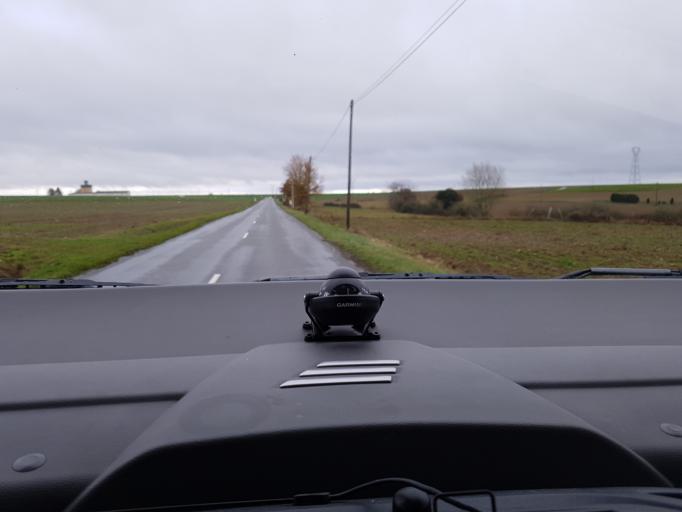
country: FR
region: Haute-Normandie
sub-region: Departement de l'Eure
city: Pont-Saint-Pierre
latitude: 49.3078
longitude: 1.3152
